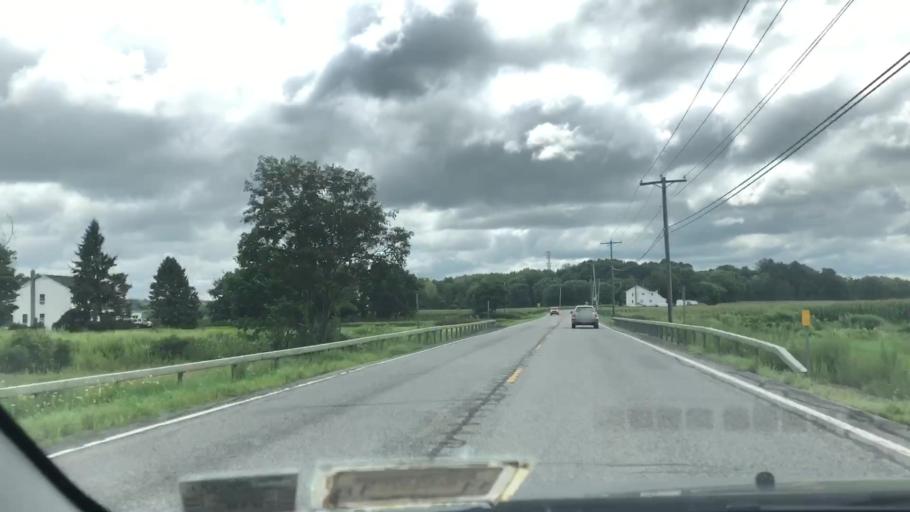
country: US
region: New York
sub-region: Wayne County
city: Macedon
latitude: 43.1002
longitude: -77.2939
